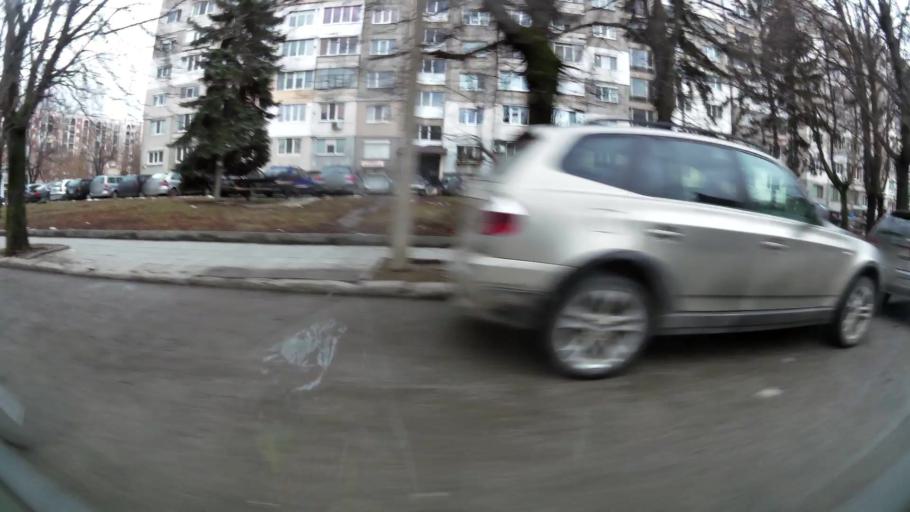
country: BG
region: Sofia-Capital
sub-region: Stolichna Obshtina
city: Sofia
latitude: 42.7270
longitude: 23.2991
